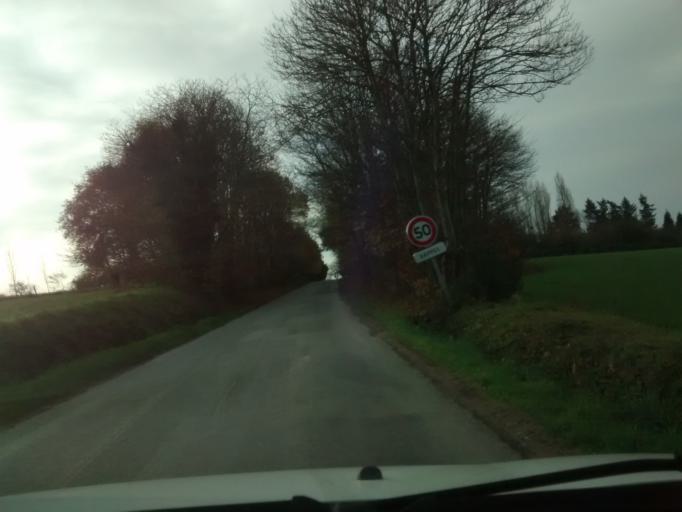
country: FR
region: Brittany
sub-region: Departement d'Ille-et-Vilaine
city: Cesson-Sevigne
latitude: 48.1000
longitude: -1.5867
